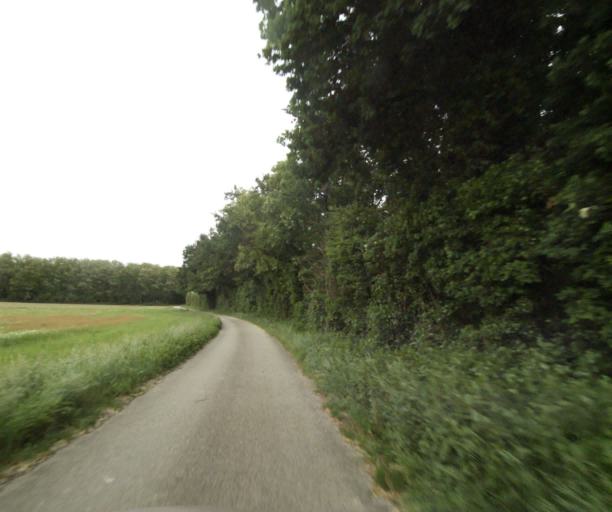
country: FR
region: Rhone-Alpes
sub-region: Departement de l'Ain
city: Mionnay
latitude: 45.8666
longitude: 4.9291
